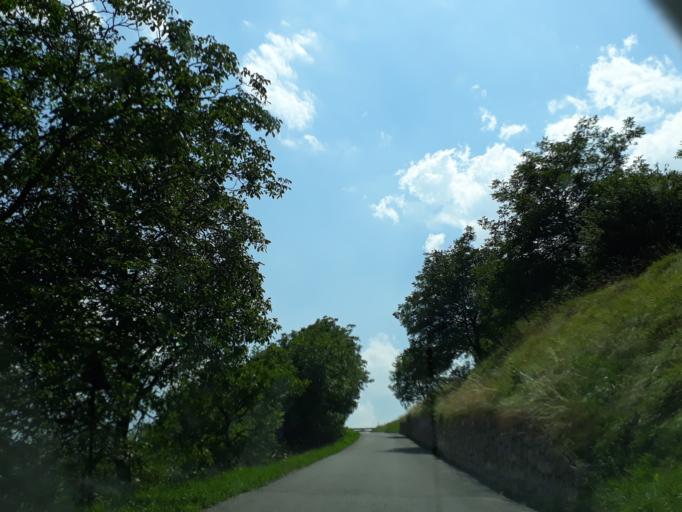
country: IT
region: Trentino-Alto Adige
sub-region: Provincia di Trento
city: Castel Condino
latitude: 45.9073
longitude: 10.5993
